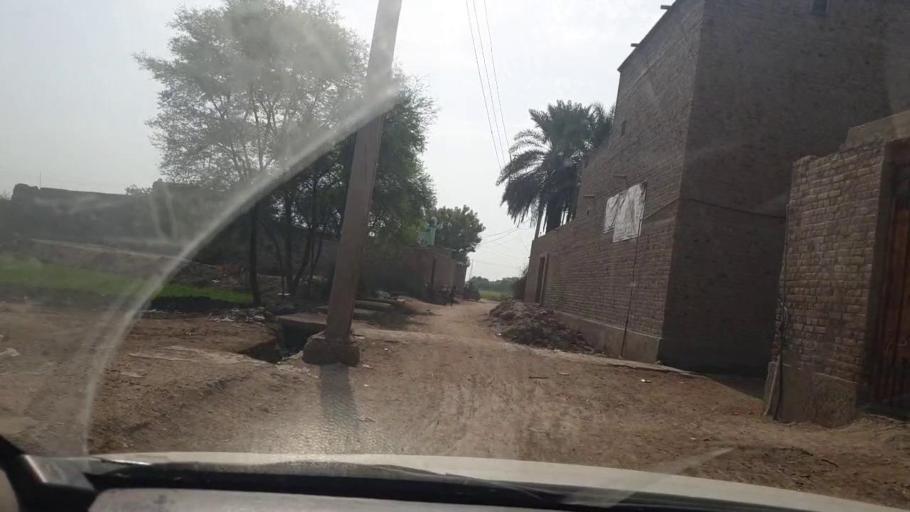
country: PK
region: Sindh
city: Lakhi
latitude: 27.8321
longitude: 68.7615
